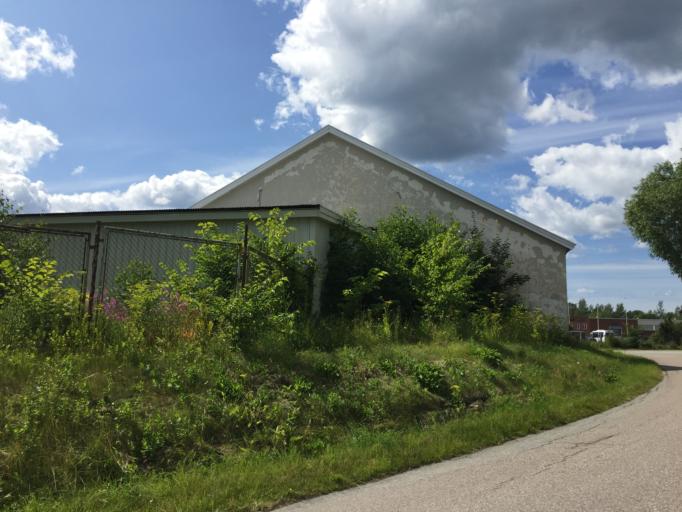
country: SE
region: Vaestmanland
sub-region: Surahammars Kommun
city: Ramnas
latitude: 59.7782
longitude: 16.1857
